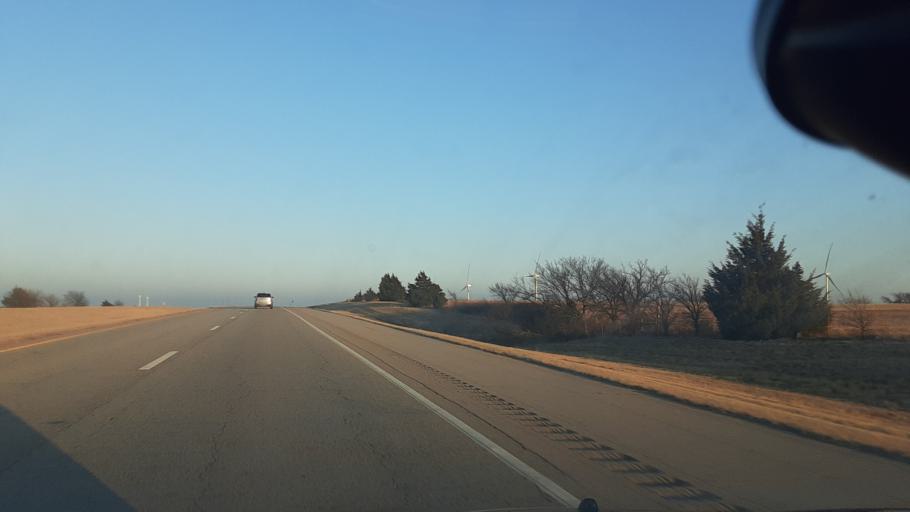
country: US
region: Oklahoma
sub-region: Noble County
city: Perry
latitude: 36.3978
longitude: -97.4383
